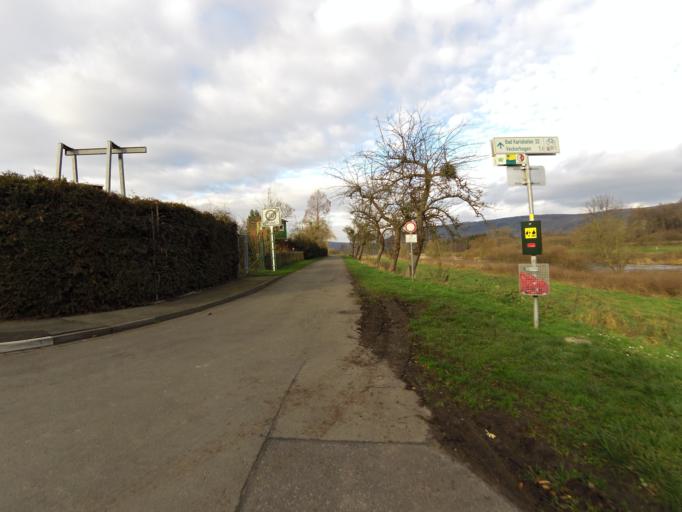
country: DE
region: Lower Saxony
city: Buhren
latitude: 51.4843
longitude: 9.6147
